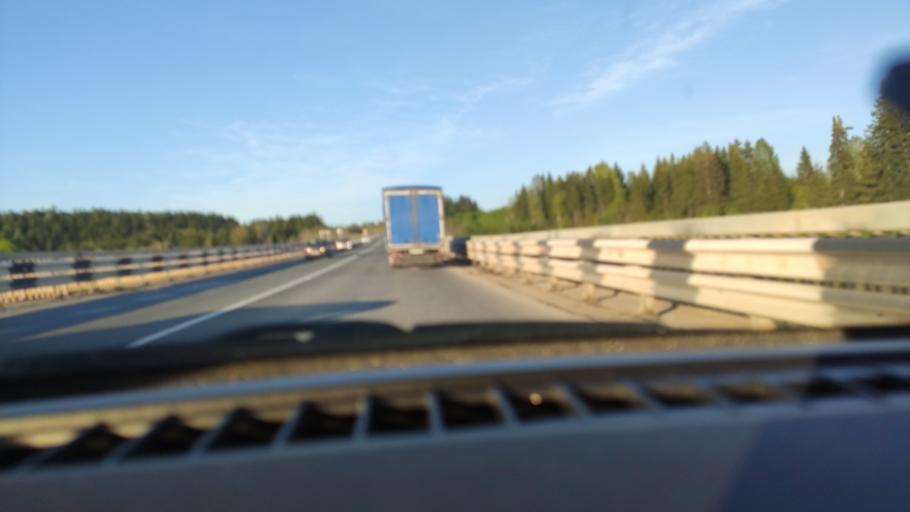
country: RU
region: Perm
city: Polazna
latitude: 58.2840
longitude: 56.4668
